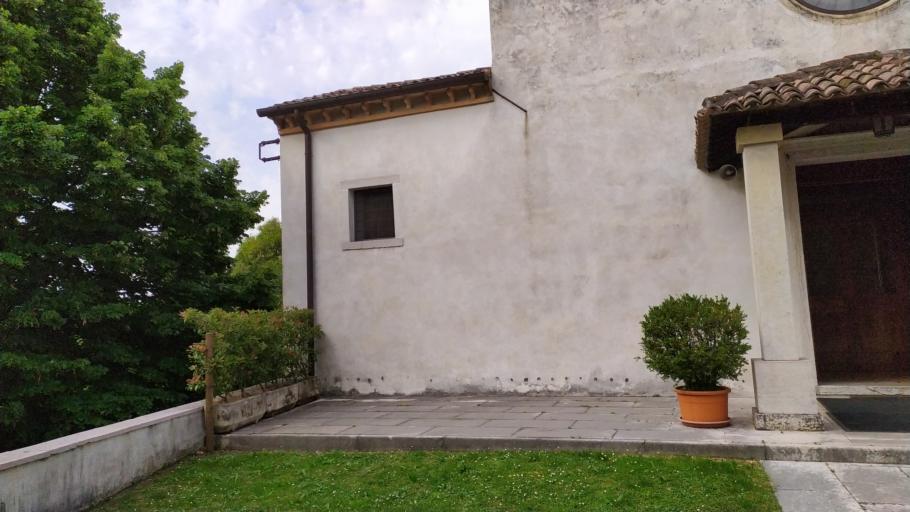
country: IT
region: Veneto
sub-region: Provincia di Treviso
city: Asolo
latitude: 45.8002
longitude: 11.9040
